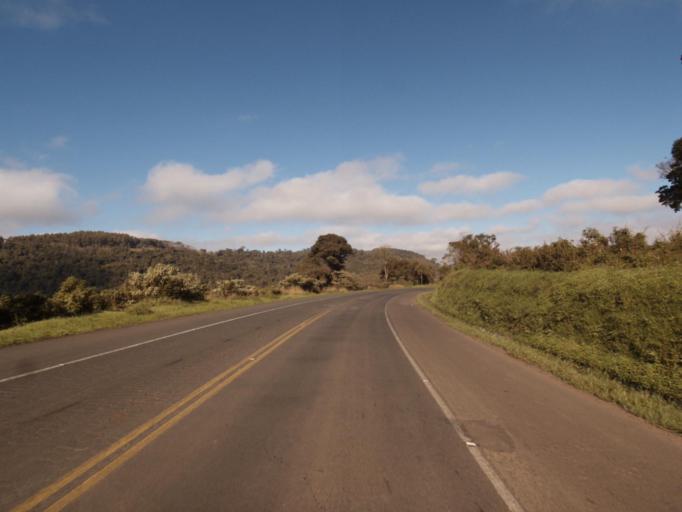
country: BR
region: Rio Grande do Sul
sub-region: Frederico Westphalen
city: Frederico Westphalen
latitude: -27.0643
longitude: -53.2212
